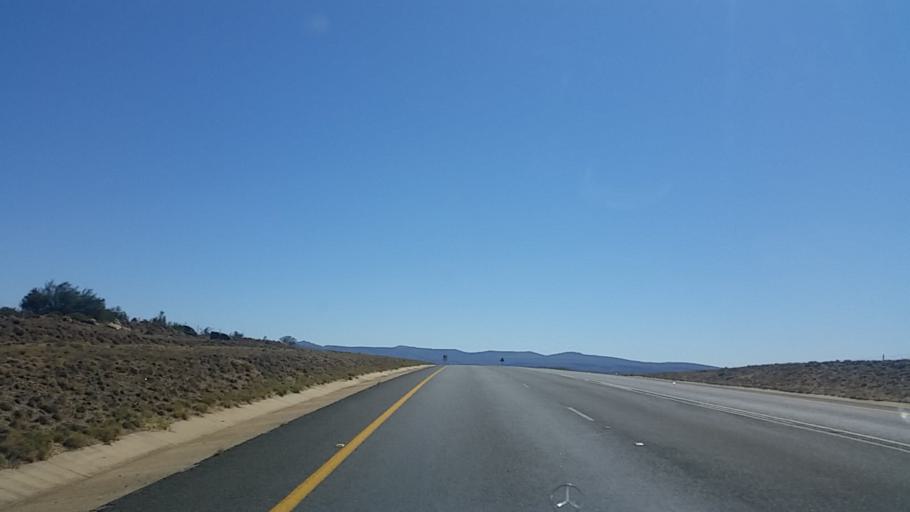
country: ZA
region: Eastern Cape
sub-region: Cacadu District Municipality
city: Graaff-Reinet
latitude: -32.0556
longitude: 24.6127
